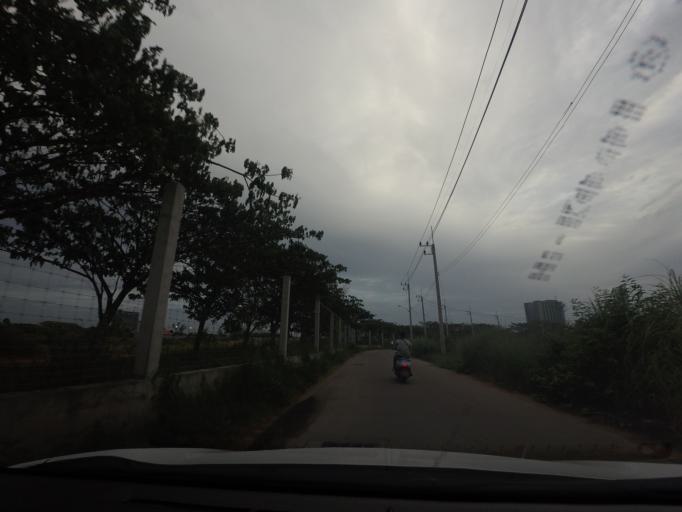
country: TH
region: Chon Buri
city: Phatthaya
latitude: 12.8999
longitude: 100.8836
